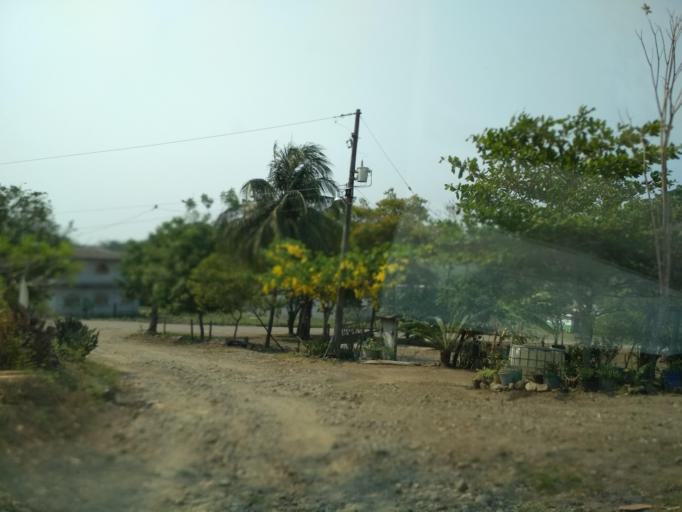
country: MX
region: Oaxaca
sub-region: Acatlan de Perez Figueroa
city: Zona Urbana Ejidal
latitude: 18.5892
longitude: -96.5614
